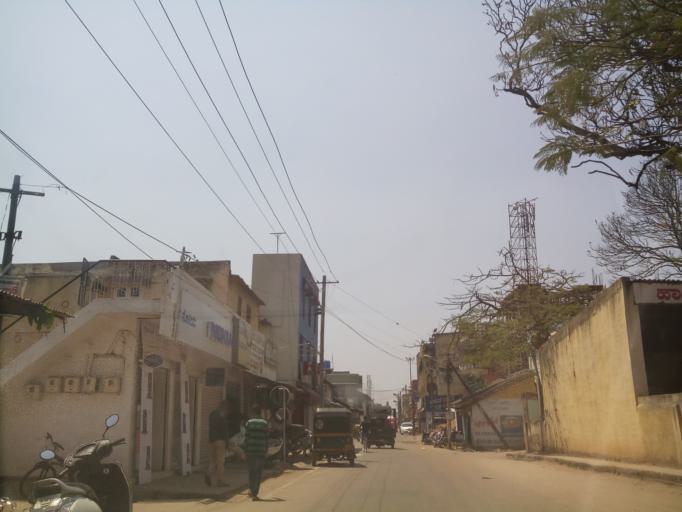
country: IN
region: Karnataka
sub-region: Hassan
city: Hassan
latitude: 13.0082
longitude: 76.0957
